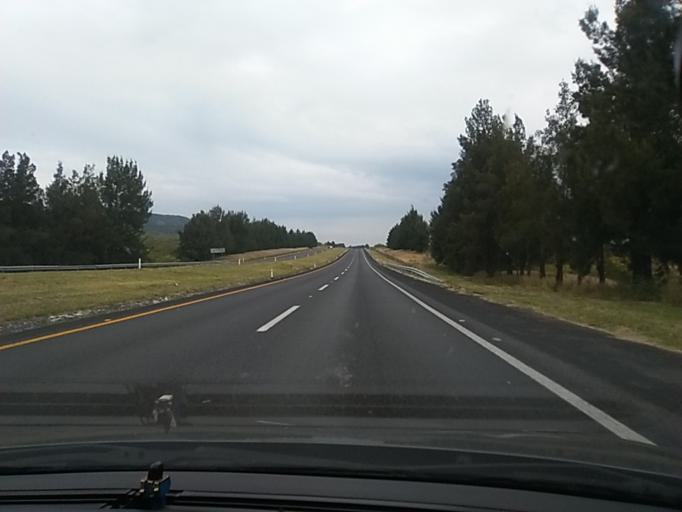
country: MX
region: Michoacan
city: Churintzio
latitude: 20.1070
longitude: -102.0365
